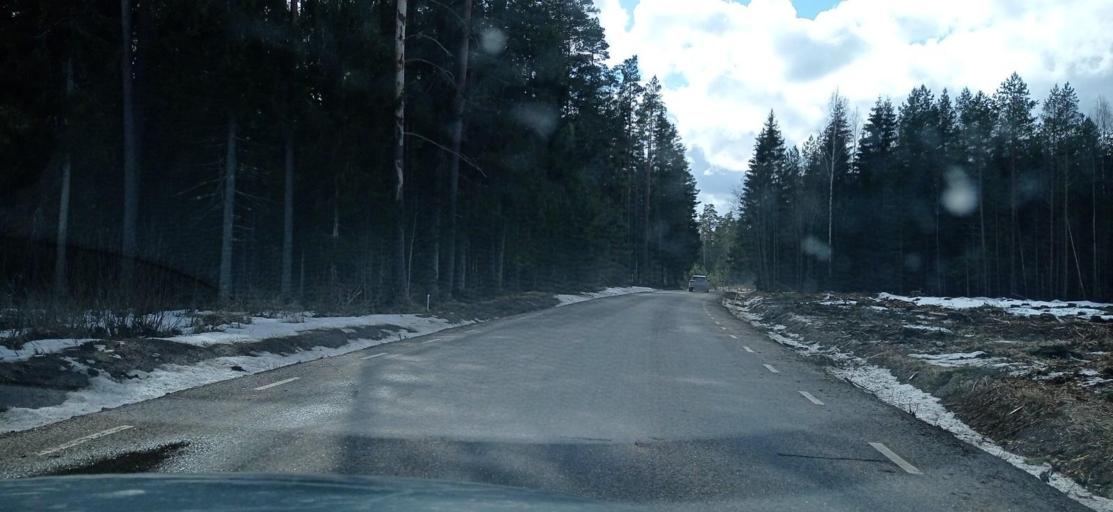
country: EE
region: Polvamaa
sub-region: Polva linn
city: Polva
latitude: 58.1469
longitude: 27.0386
